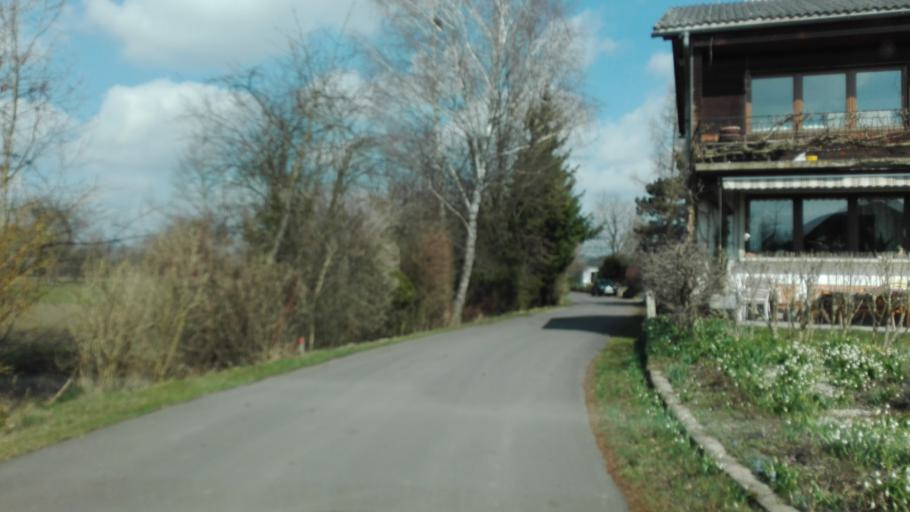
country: AT
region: Upper Austria
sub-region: Politischer Bezirk Urfahr-Umgebung
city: Goldworth
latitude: 48.3277
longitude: 14.0948
